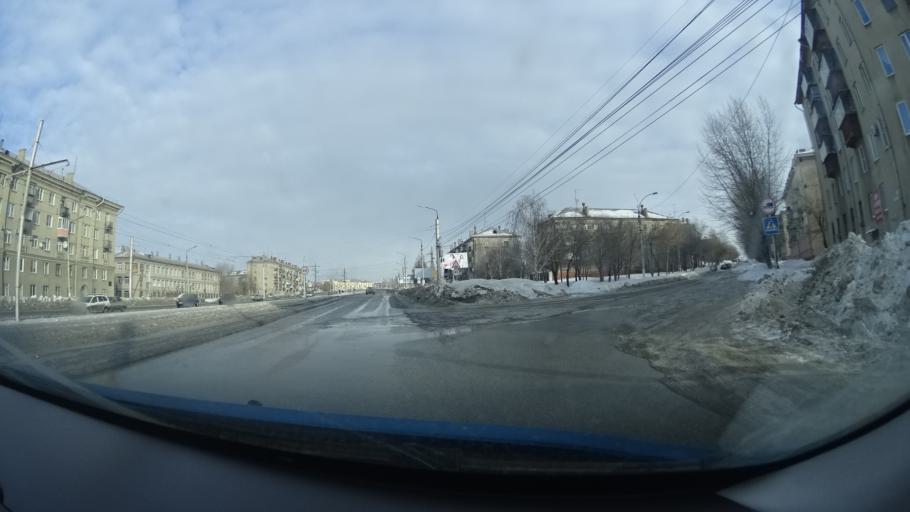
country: RU
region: Chelyabinsk
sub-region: Gorod Magnitogorsk
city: Magnitogorsk
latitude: 53.4343
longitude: 58.9841
